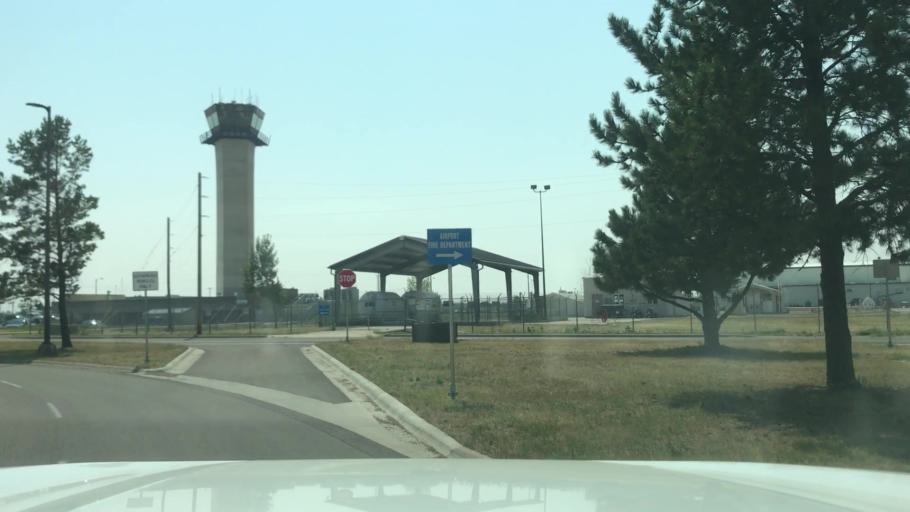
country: US
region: Montana
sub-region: Cascade County
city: Great Falls
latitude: 47.4814
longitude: -111.3594
